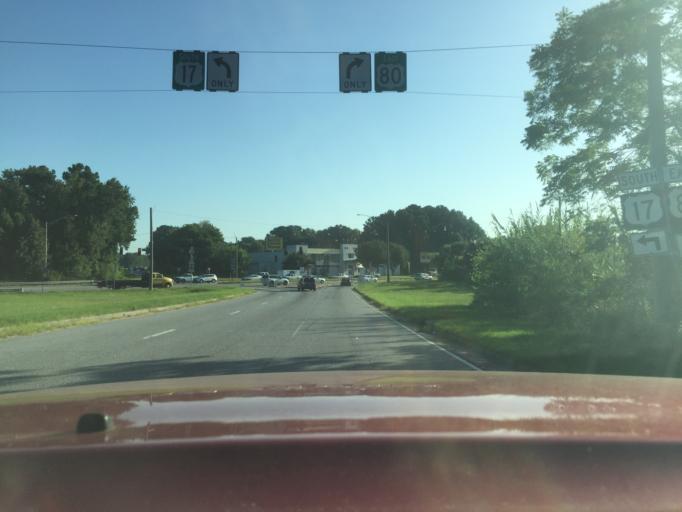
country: US
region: Georgia
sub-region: Chatham County
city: Savannah
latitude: 32.0531
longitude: -81.1413
